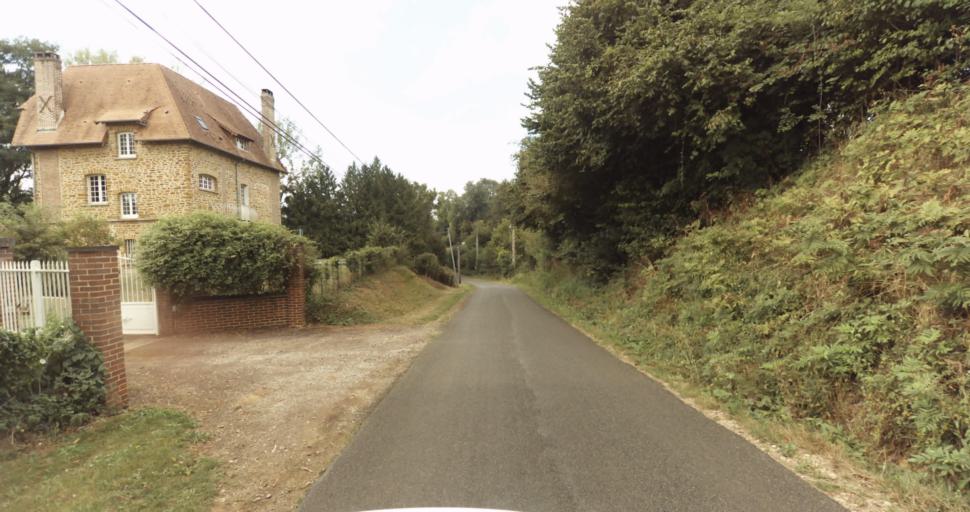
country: FR
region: Lower Normandy
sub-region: Departement de l'Orne
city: Vimoutiers
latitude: 48.9123
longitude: 0.2125
